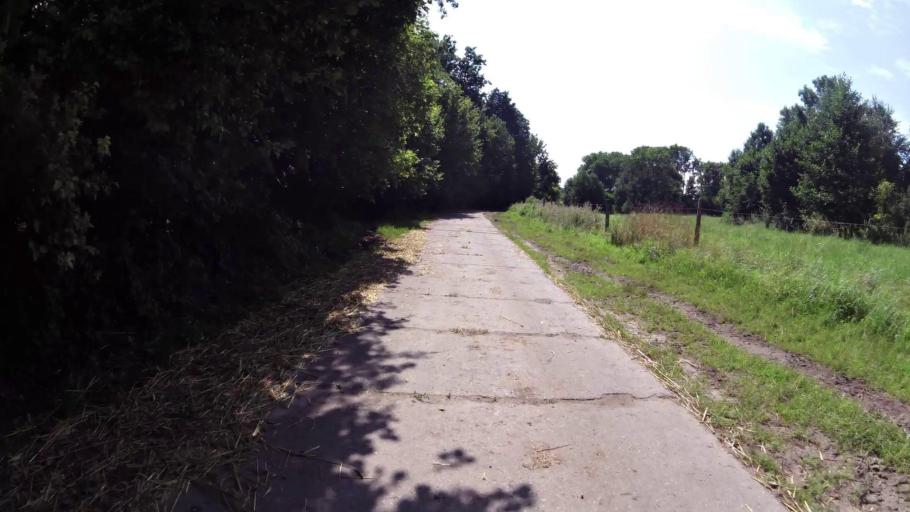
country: PL
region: West Pomeranian Voivodeship
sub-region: Powiat stargardzki
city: Suchan
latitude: 53.2572
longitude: 15.3982
